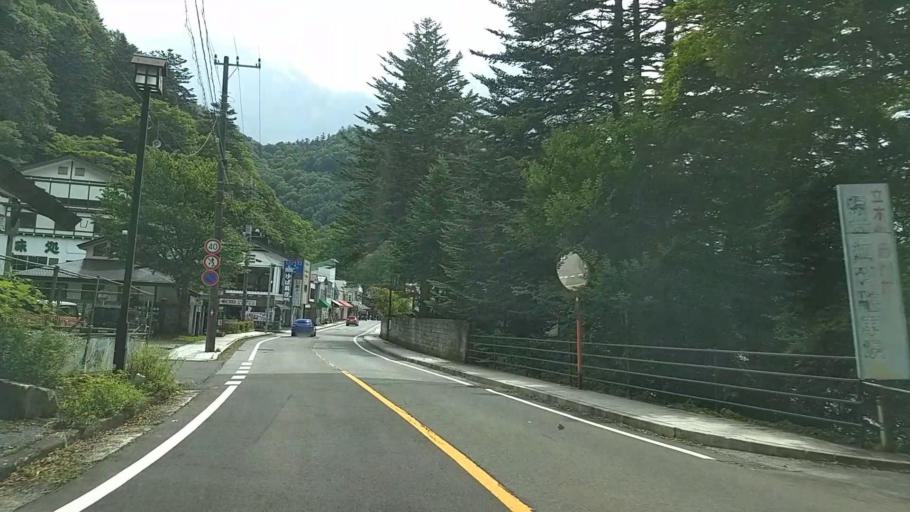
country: JP
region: Tochigi
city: Nikko
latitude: 36.7337
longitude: 139.4924
